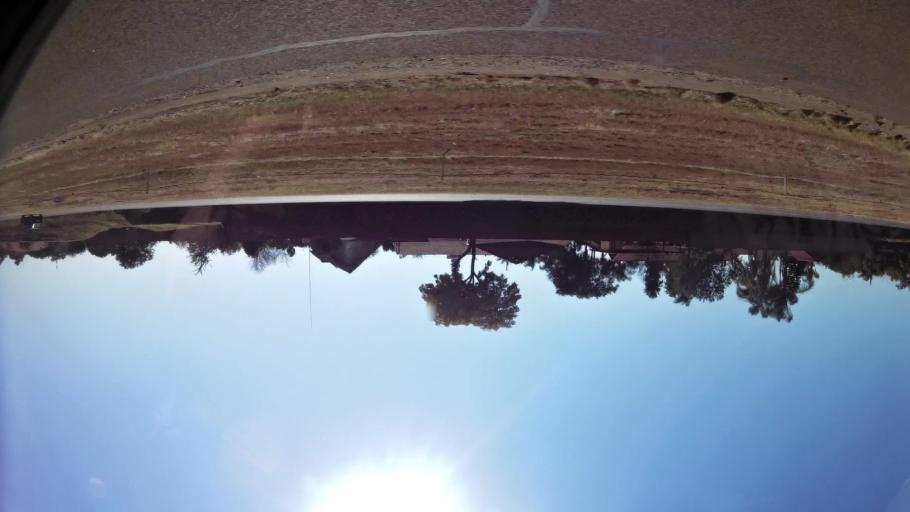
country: ZA
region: Gauteng
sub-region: City of Tshwane Metropolitan Municipality
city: Pretoria
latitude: -25.6539
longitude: 28.1209
